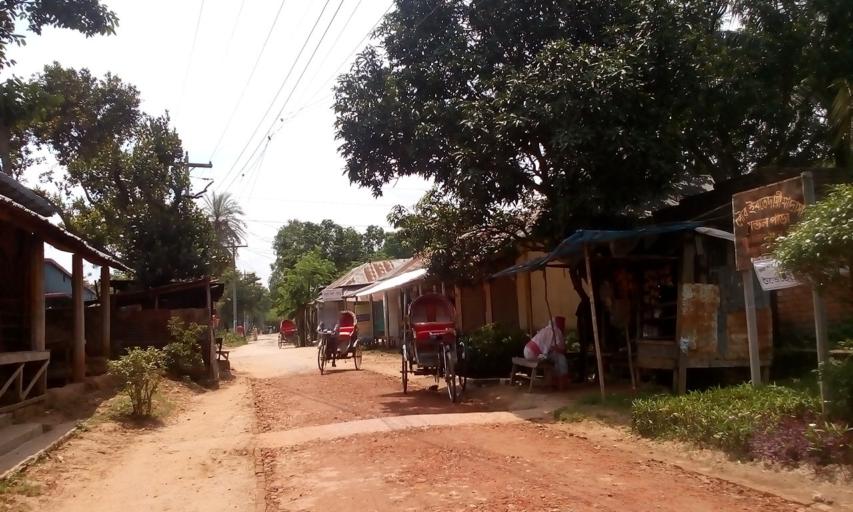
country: BD
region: Rangpur Division
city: Parbatipur
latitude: 25.3994
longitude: 88.9908
